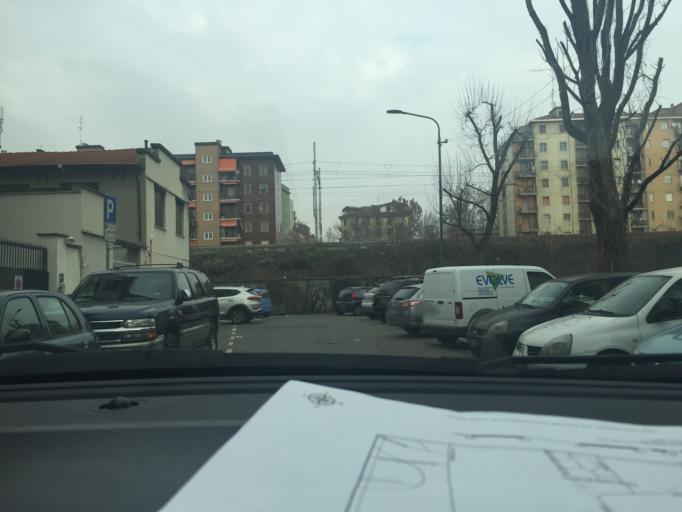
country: IT
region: Lombardy
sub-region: Citta metropolitana di Milano
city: Milano
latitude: 45.4425
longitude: 9.1739
